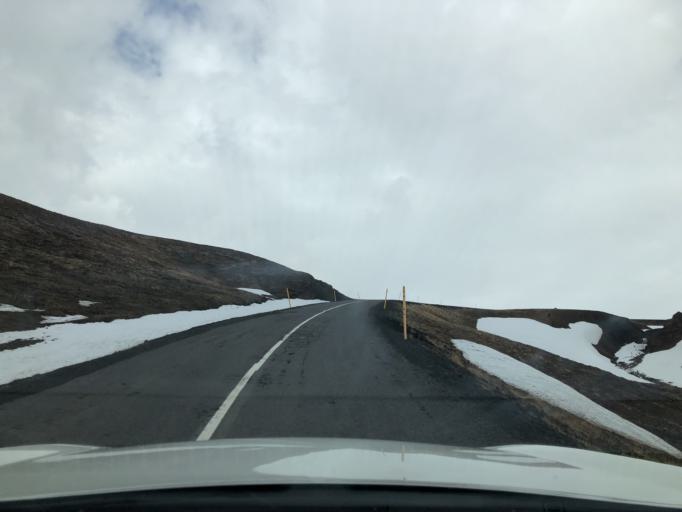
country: IS
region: Northeast
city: Laugar
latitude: 65.7100
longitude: -16.7727
